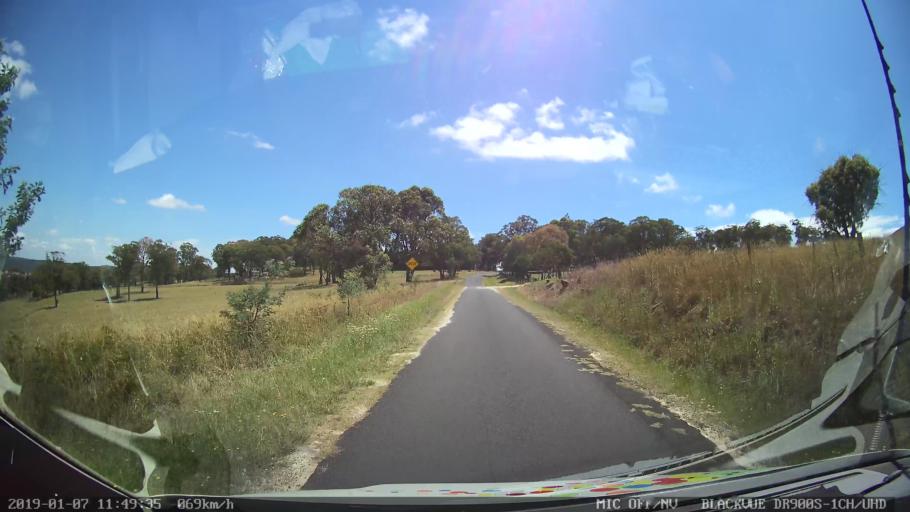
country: AU
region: New South Wales
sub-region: Guyra
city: Guyra
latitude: -30.3175
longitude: 151.6291
